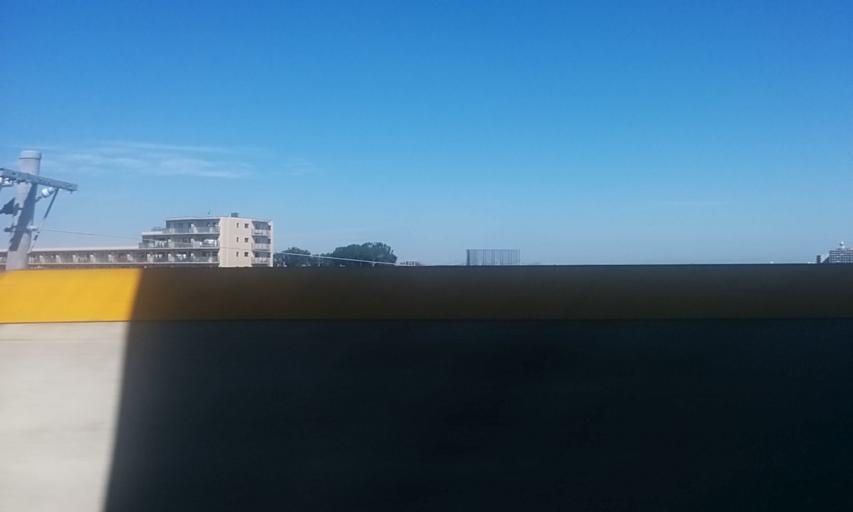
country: JP
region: Chiba
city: Nagareyama
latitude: 35.8772
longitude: 139.9307
